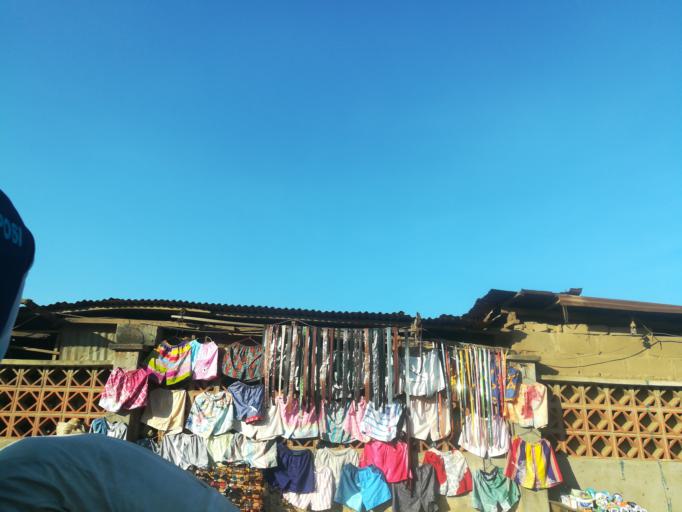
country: NG
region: Lagos
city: Ikorodu
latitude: 6.5891
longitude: 3.5183
